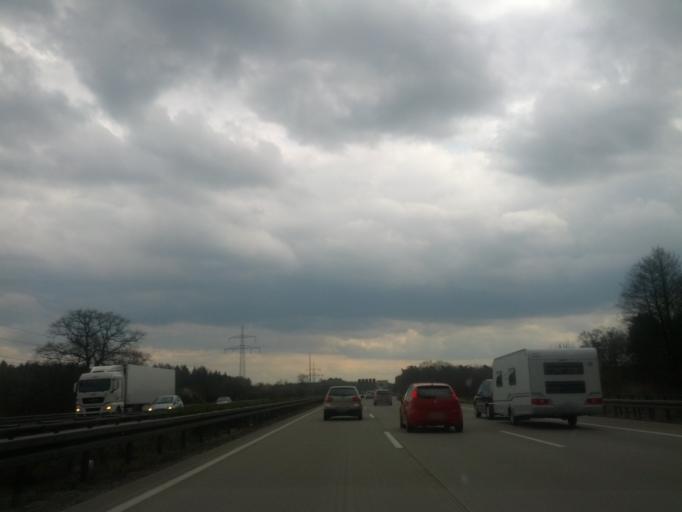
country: DE
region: Lower Saxony
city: Isernhagen Farster Bauerschaft
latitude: 52.5294
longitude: 9.8106
